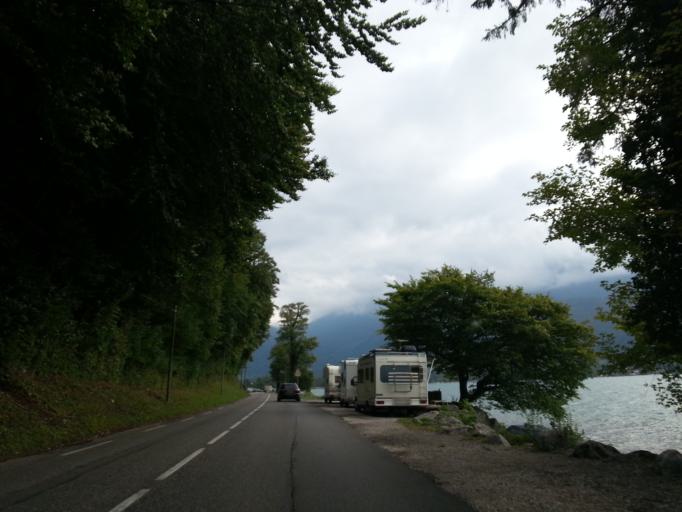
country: FR
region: Rhone-Alpes
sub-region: Departement de la Haute-Savoie
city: Doussard
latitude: 45.8031
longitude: 6.2301
